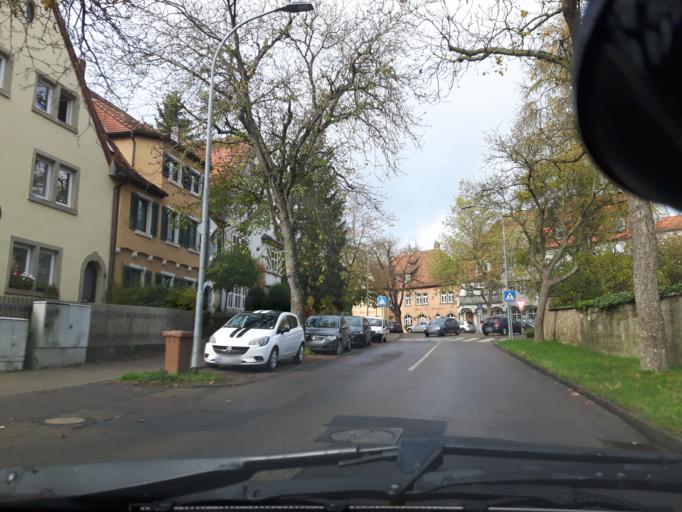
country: DE
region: Bavaria
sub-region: Regierungsbezirk Mittelfranken
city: Rothenburg ob der Tauber
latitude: 49.3757
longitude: 10.1860
